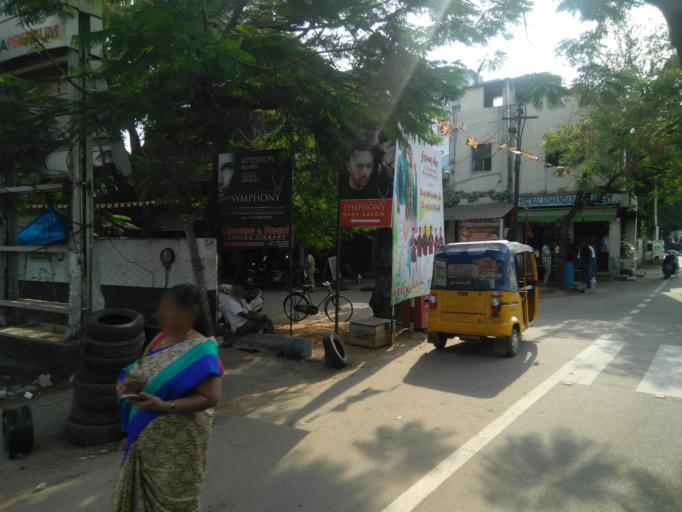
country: IN
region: Tamil Nadu
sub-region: Coimbatore
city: Coimbatore
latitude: 10.9955
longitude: 76.9758
